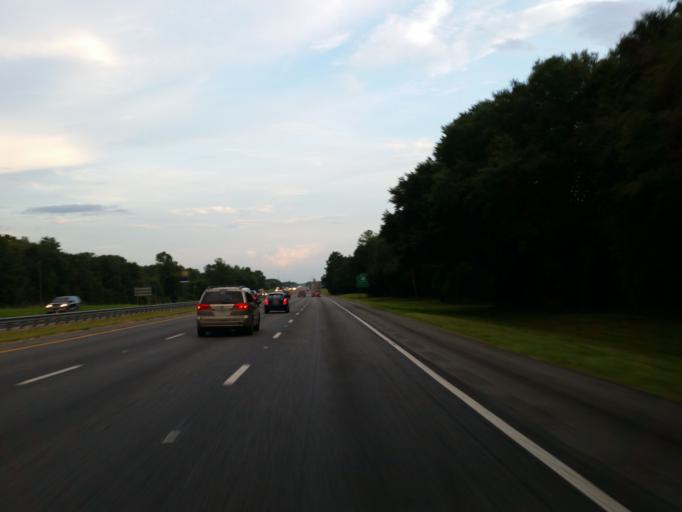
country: US
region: Florida
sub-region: Columbia County
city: Lake City
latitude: 30.1338
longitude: -82.6652
